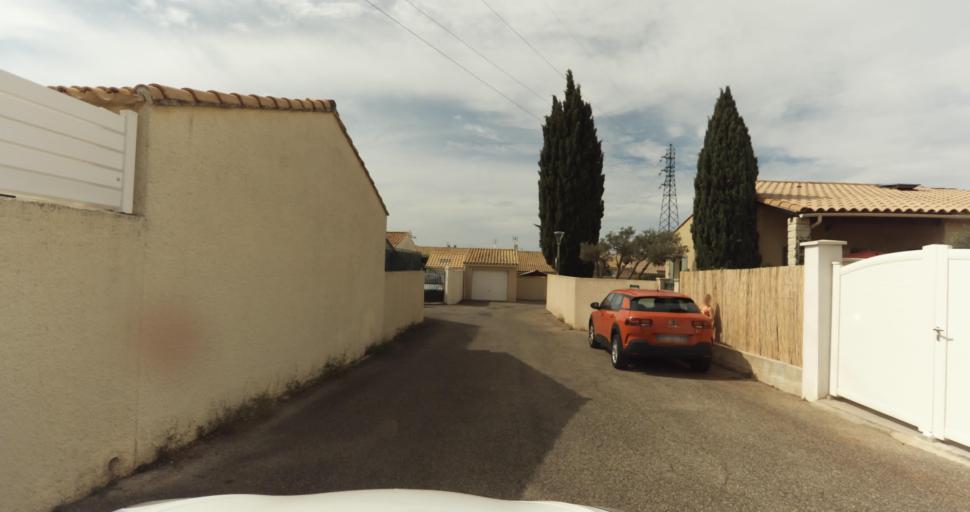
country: FR
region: Provence-Alpes-Cote d'Azur
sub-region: Departement des Bouches-du-Rhone
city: Miramas
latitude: 43.5717
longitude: 4.9987
